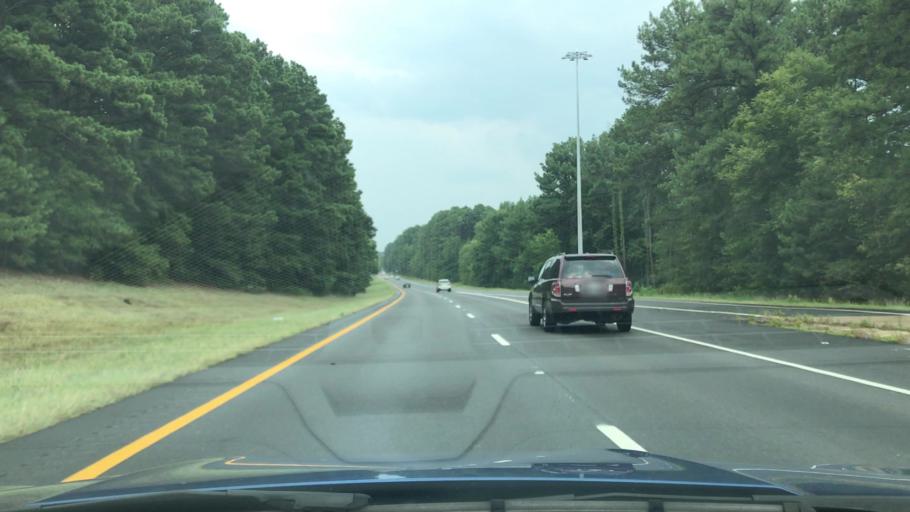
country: US
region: Texas
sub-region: Harrison County
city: Hallsville
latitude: 32.4864
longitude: -94.4662
